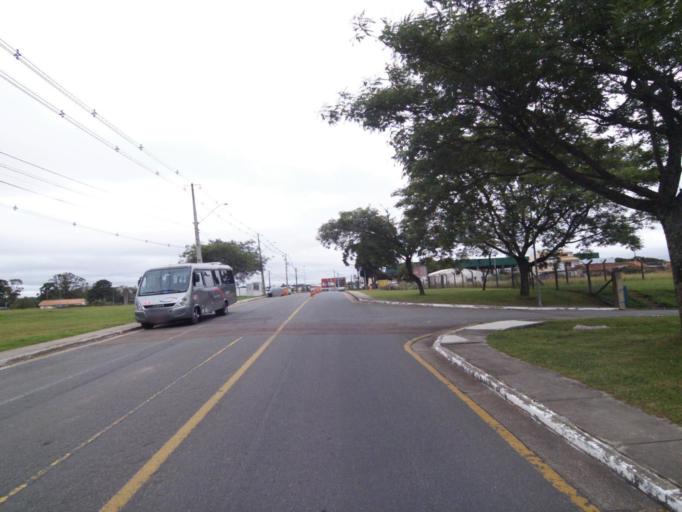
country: BR
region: Parana
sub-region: Sao Jose Dos Pinhais
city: Sao Jose dos Pinhais
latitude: -25.5349
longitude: -49.1795
